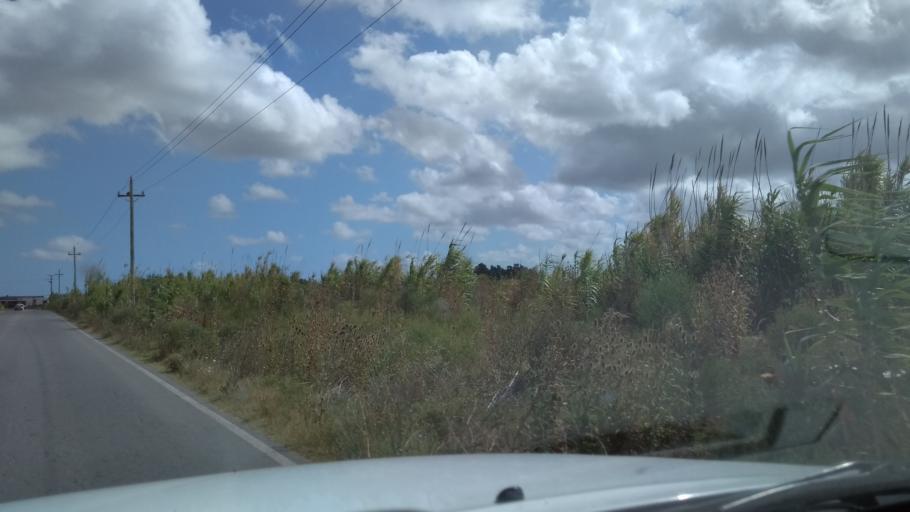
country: UY
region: Canelones
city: Colonia Nicolich
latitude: -34.7808
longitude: -56.0191
